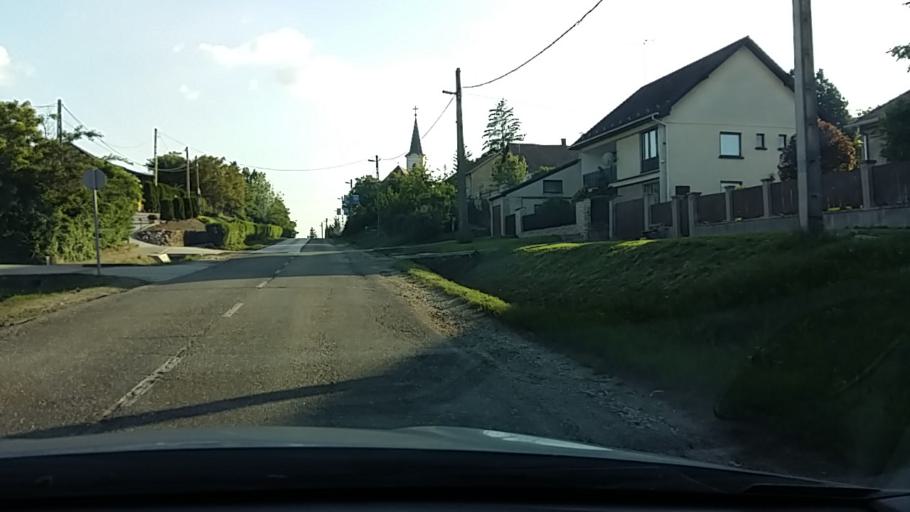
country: HU
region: Pest
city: Kosd
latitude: 47.7936
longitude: 19.2195
